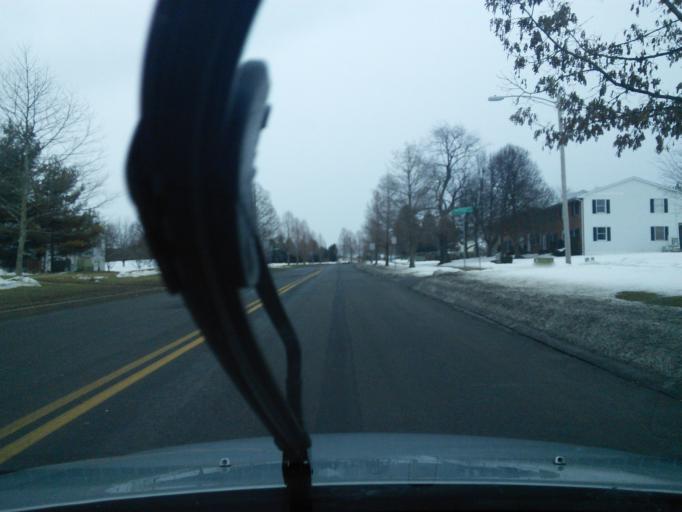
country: US
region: Pennsylvania
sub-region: Centre County
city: State College
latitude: 40.7718
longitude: -77.8651
